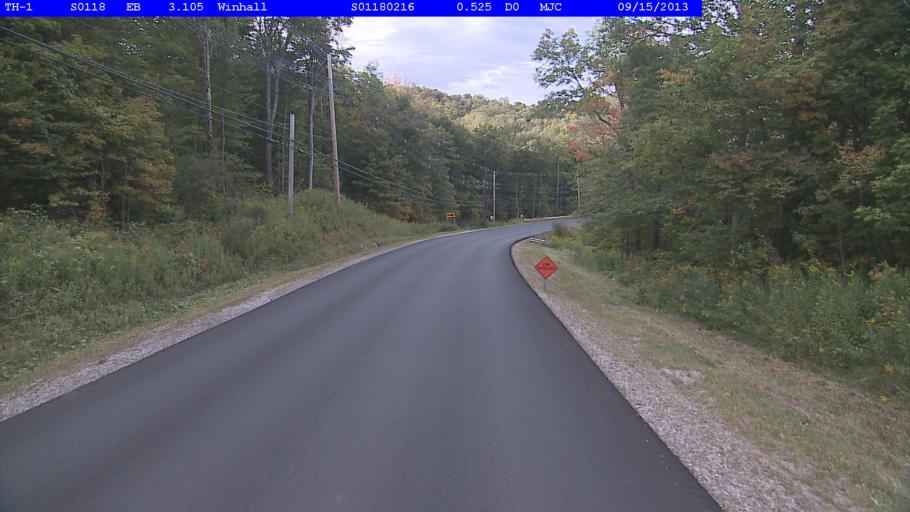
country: US
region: Vermont
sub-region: Bennington County
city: Manchester Center
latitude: 43.1225
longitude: -72.9128
